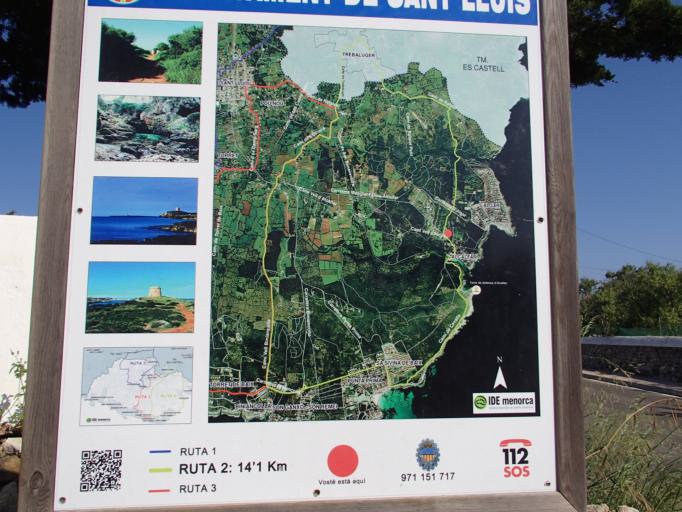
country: ES
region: Balearic Islands
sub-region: Illes Balears
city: Sant Lluis
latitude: 39.8320
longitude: 4.2916
